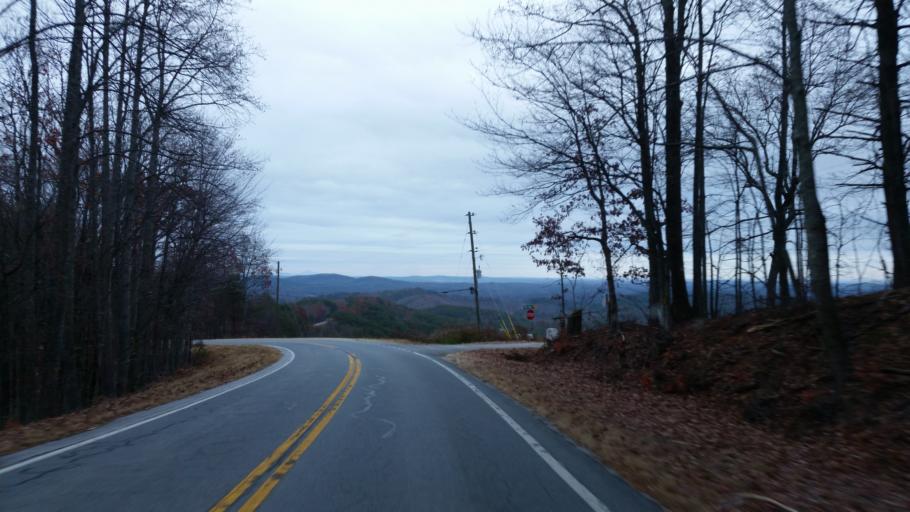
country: US
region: Georgia
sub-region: Pickens County
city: Jasper
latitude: 34.5352
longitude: -84.2990
